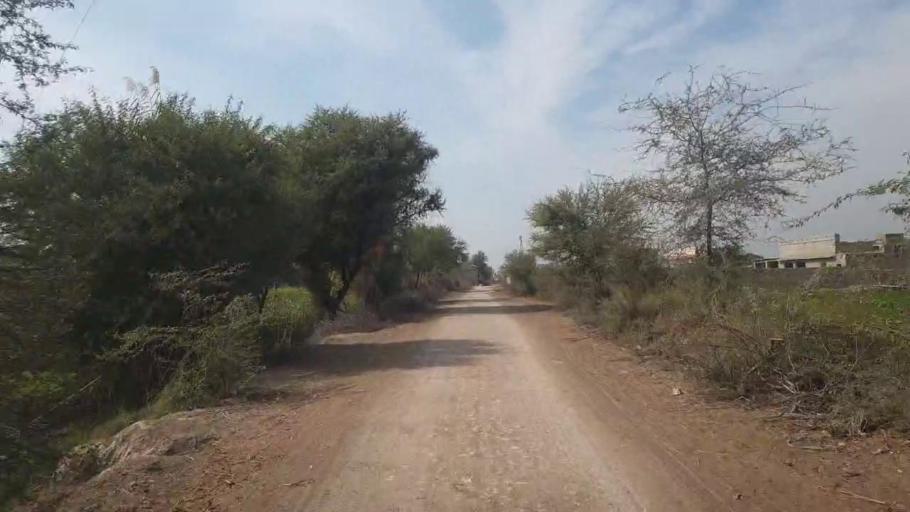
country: PK
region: Sindh
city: Nawabshah
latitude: 26.1444
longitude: 68.4992
